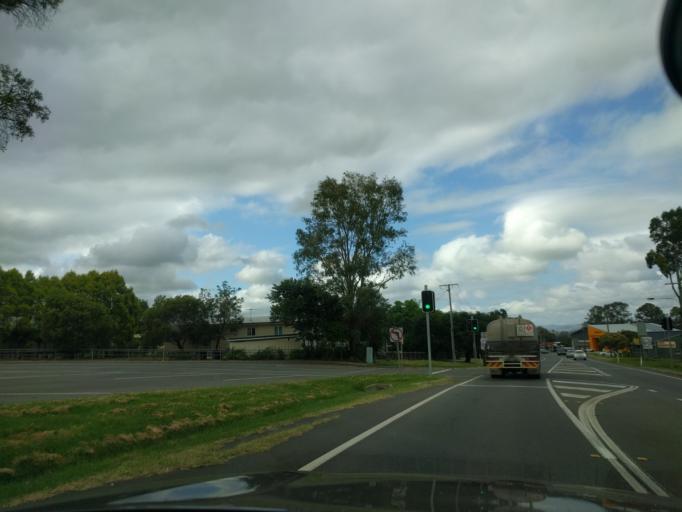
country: AU
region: Queensland
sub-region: Logan
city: Cedar Vale
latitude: -27.9722
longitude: 152.9961
